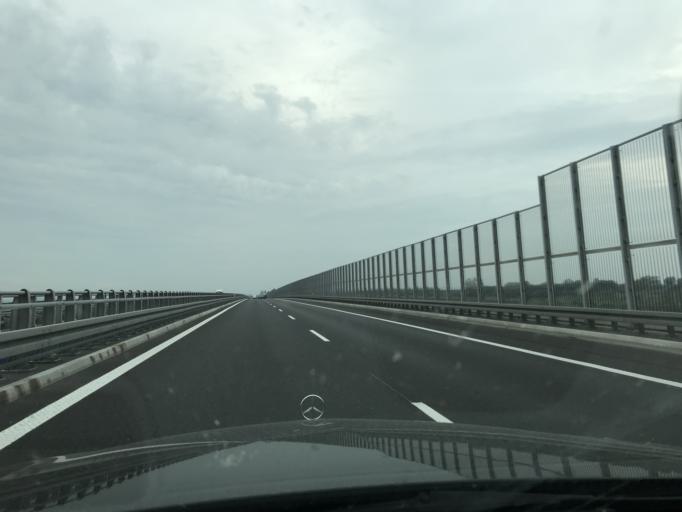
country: PL
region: Lesser Poland Voivodeship
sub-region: Powiat tarnowski
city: Niedomice
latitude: 50.0542
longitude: 20.9145
